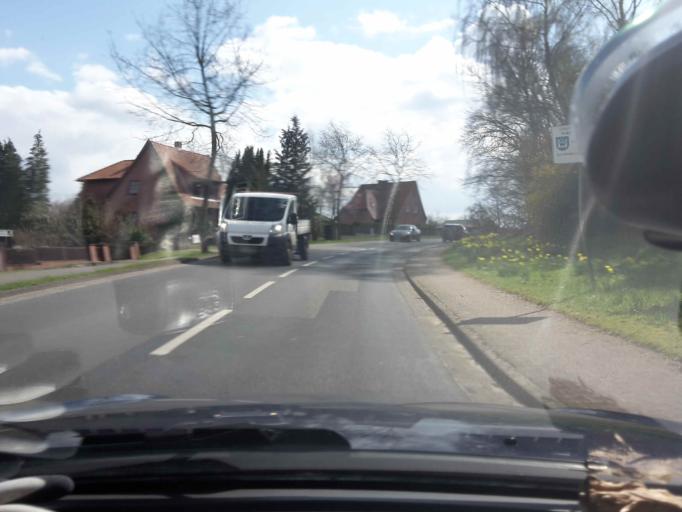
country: DE
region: Lower Saxony
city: Jesteburg
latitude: 53.2953
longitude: 9.9738
